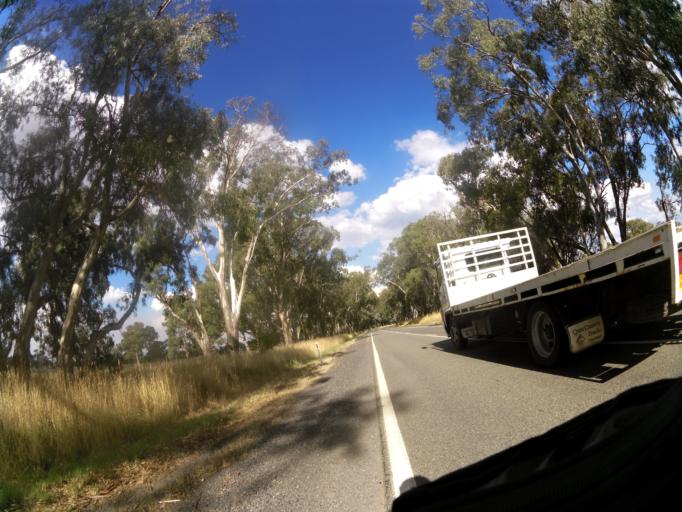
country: AU
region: Victoria
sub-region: Mansfield
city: Mansfield
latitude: -37.0027
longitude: 146.0759
